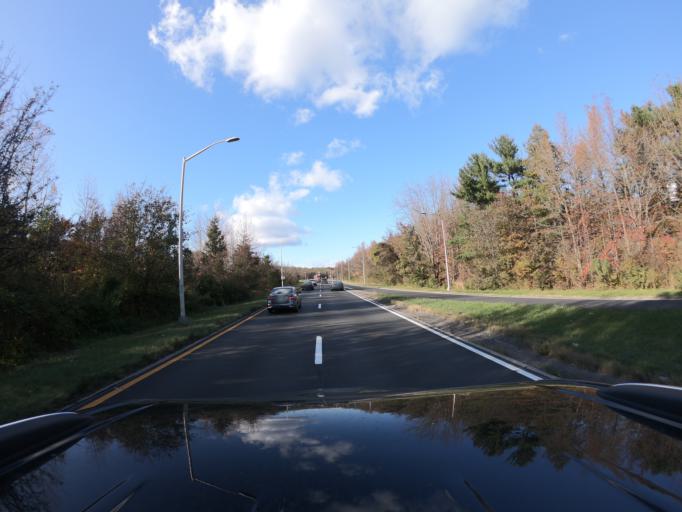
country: US
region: New Jersey
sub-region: Middlesex County
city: Sewaren
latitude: 40.5287
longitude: -74.2219
